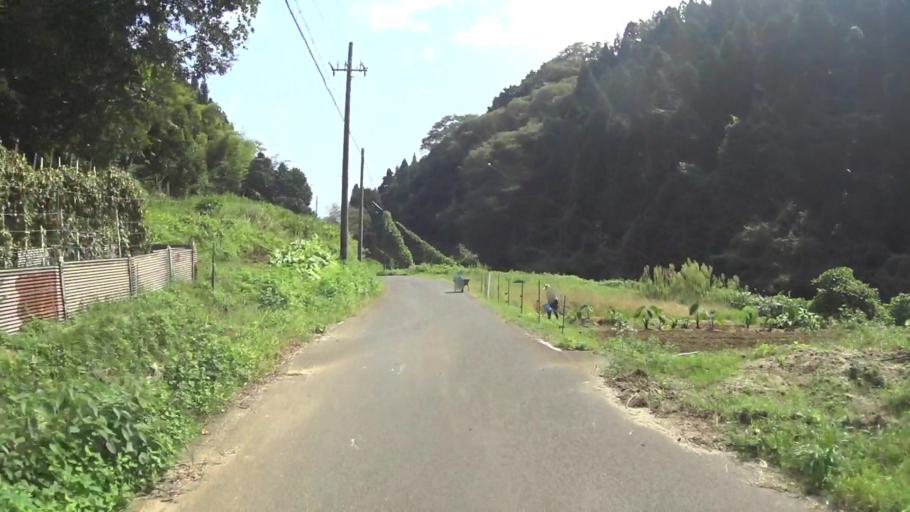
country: JP
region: Kyoto
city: Miyazu
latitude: 35.6557
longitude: 135.2542
